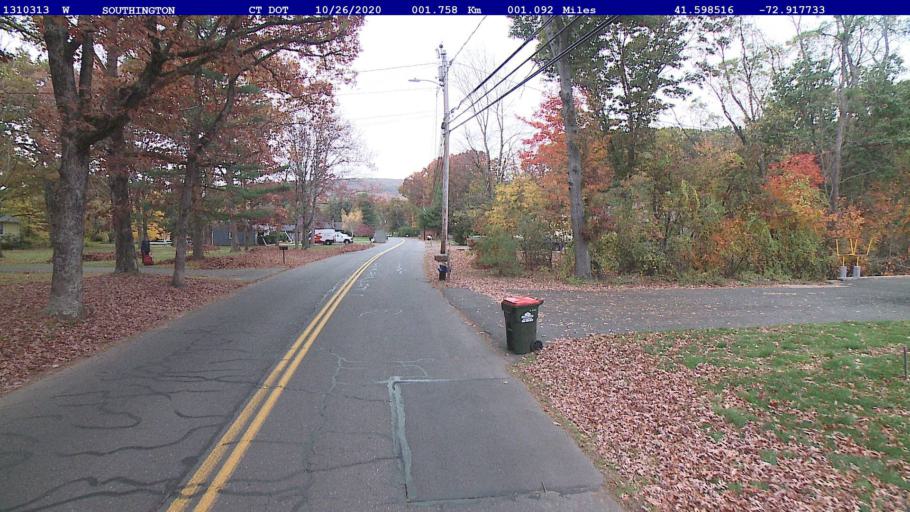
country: US
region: Connecticut
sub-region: New Haven County
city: Wolcott
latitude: 41.5985
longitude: -72.9178
